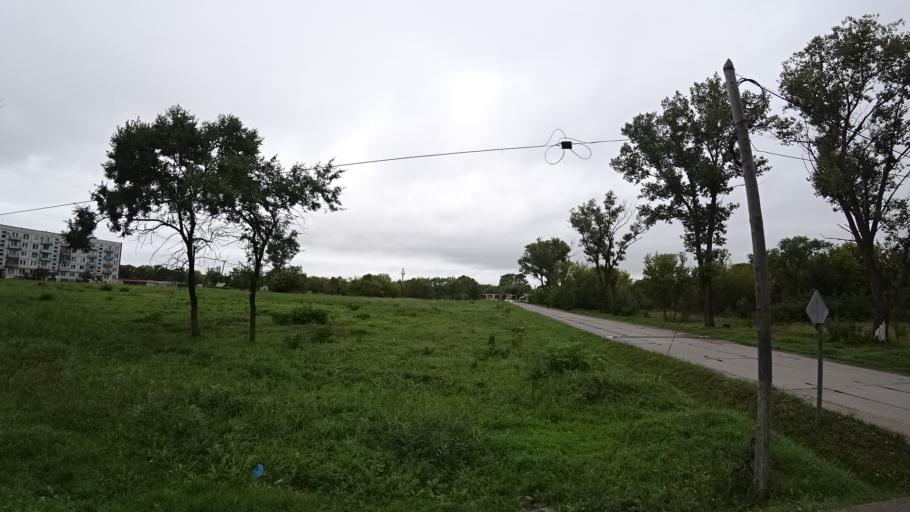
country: RU
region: Primorskiy
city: Chernigovka
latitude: 44.3315
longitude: 132.5336
